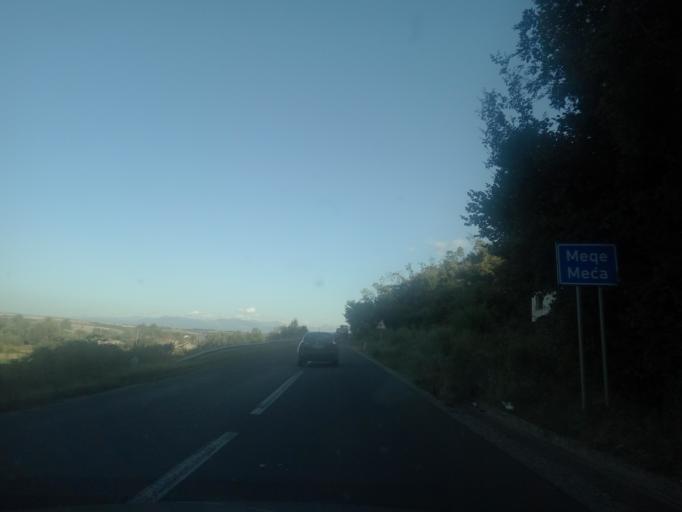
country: XK
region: Gjakova
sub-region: Komuna e Gjakoves
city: Gjakove
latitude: 42.4603
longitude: 20.5058
